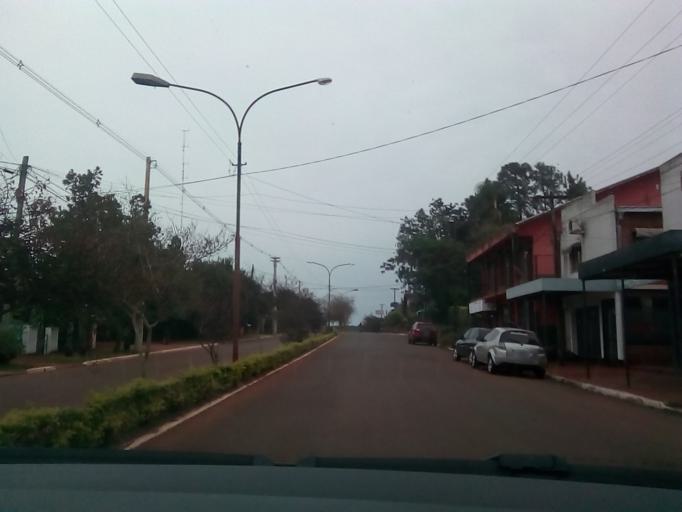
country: AR
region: Misiones
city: Puerto Esperanza
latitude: -26.0228
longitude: -54.6167
